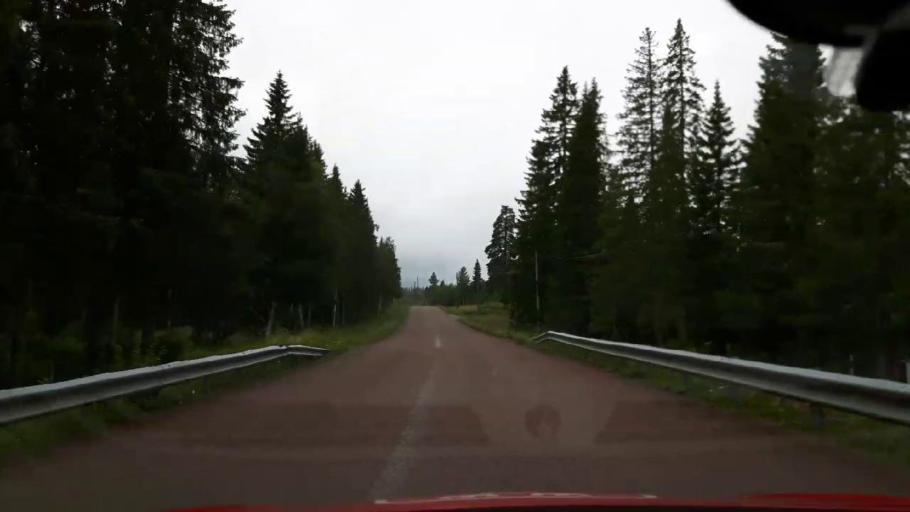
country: SE
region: Jaemtland
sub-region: Krokoms Kommun
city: Valla
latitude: 63.3905
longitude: 13.8403
